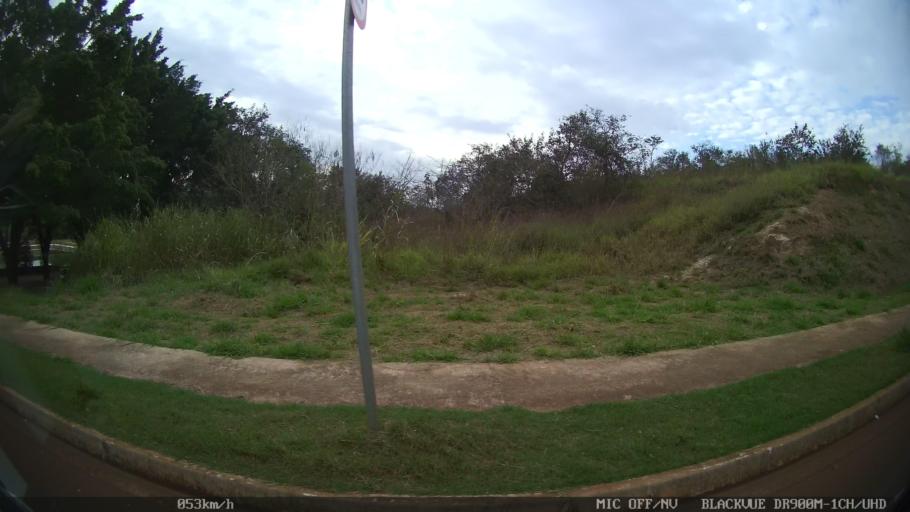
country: BR
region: Sao Paulo
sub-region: Americana
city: Americana
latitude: -22.6511
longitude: -47.3492
